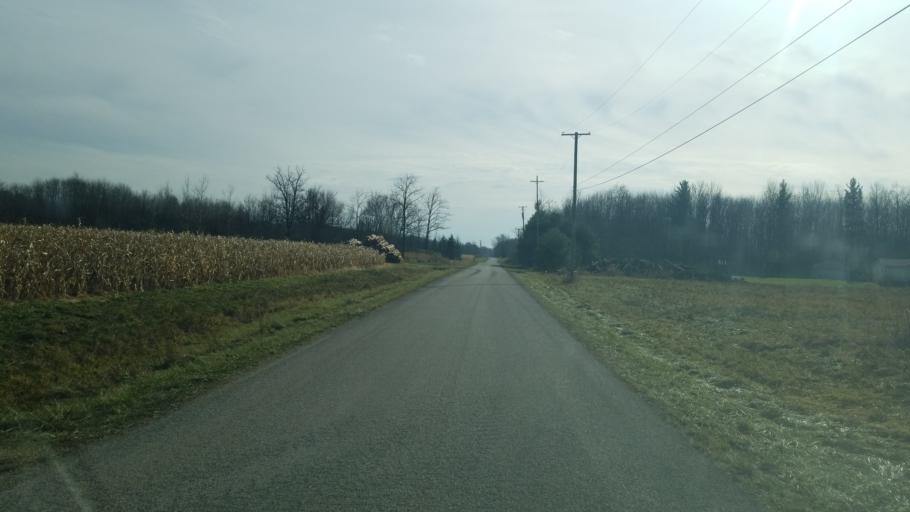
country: US
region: Ohio
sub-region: Ashtabula County
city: Roaming Shores
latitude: 41.6831
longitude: -80.9306
